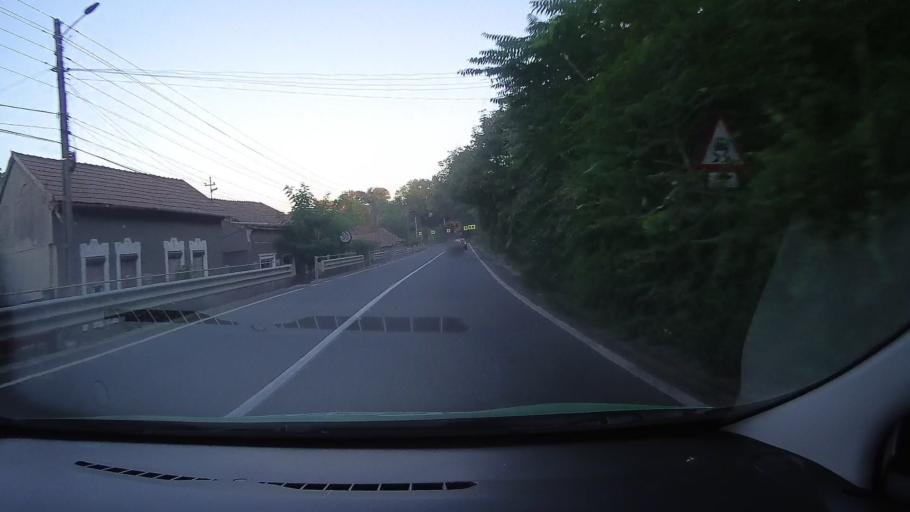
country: RO
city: Szekelyhid
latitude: 47.3533
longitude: 22.1036
